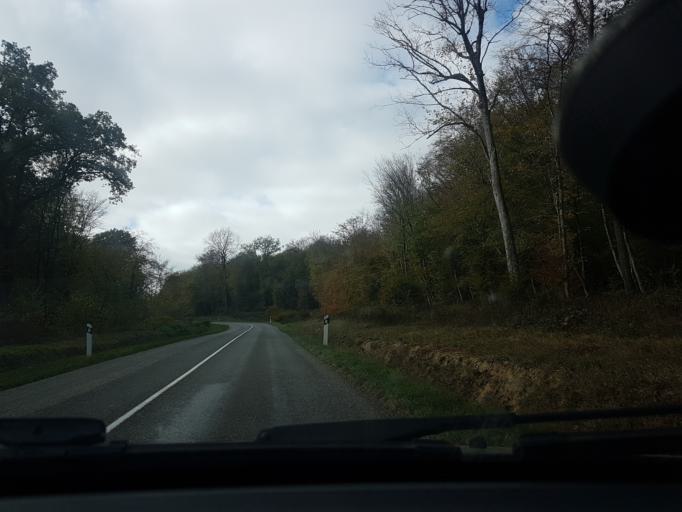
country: FR
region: Franche-Comte
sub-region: Territoire de Belfort
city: Essert
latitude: 47.6492
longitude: 6.8177
